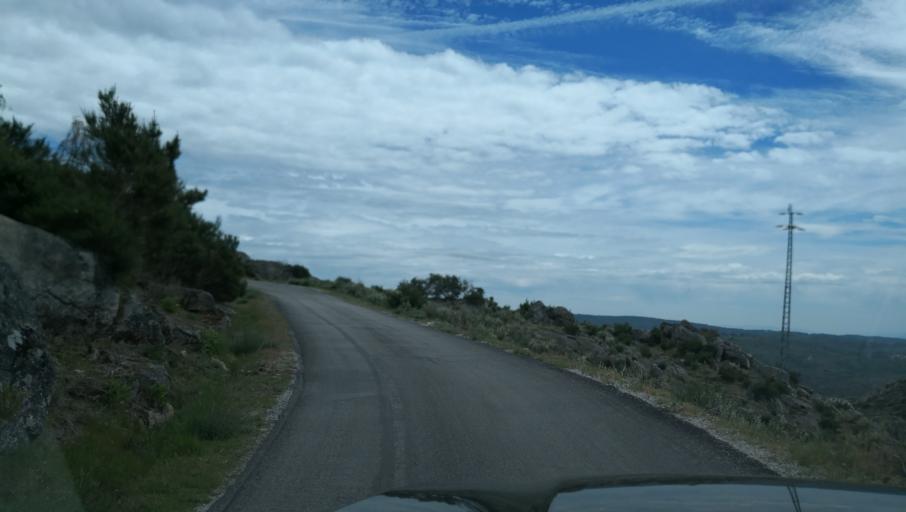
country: PT
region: Vila Real
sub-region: Vila Real
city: Vila Real
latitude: 41.3745
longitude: -7.6879
